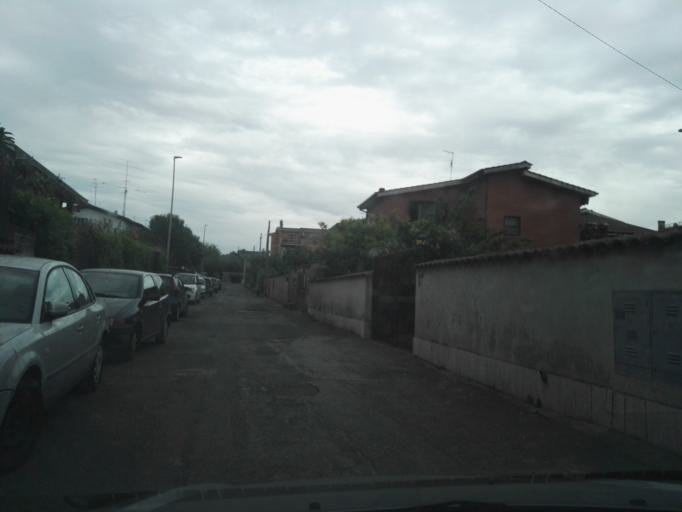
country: IT
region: Latium
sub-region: Citta metropolitana di Roma Capitale
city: Selcetta
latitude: 41.7708
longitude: 12.4807
